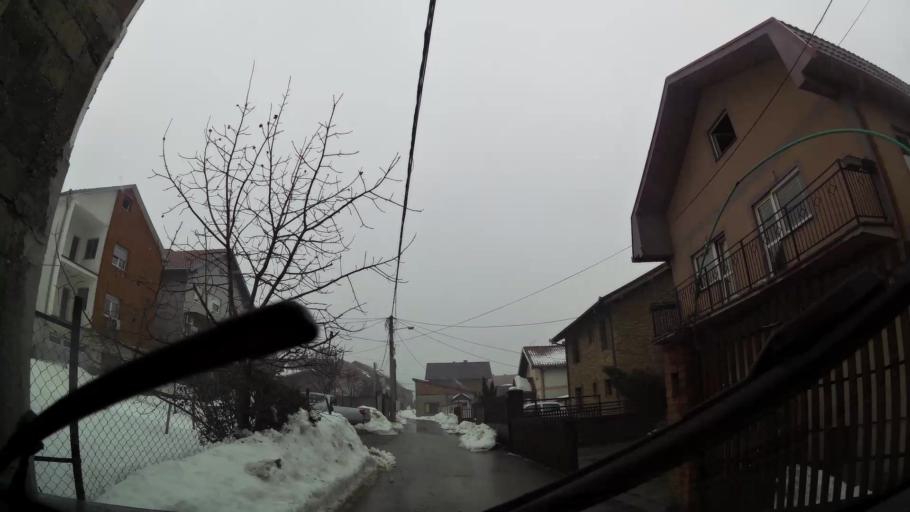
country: RS
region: Central Serbia
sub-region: Belgrade
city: Zvezdara
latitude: 44.7696
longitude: 20.5329
